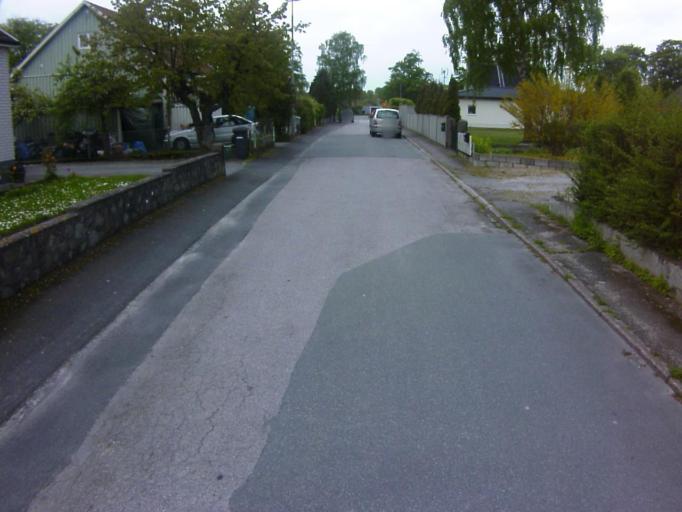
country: SE
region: Blekinge
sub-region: Solvesborgs Kommun
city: Soelvesborg
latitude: 56.0477
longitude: 14.5743
